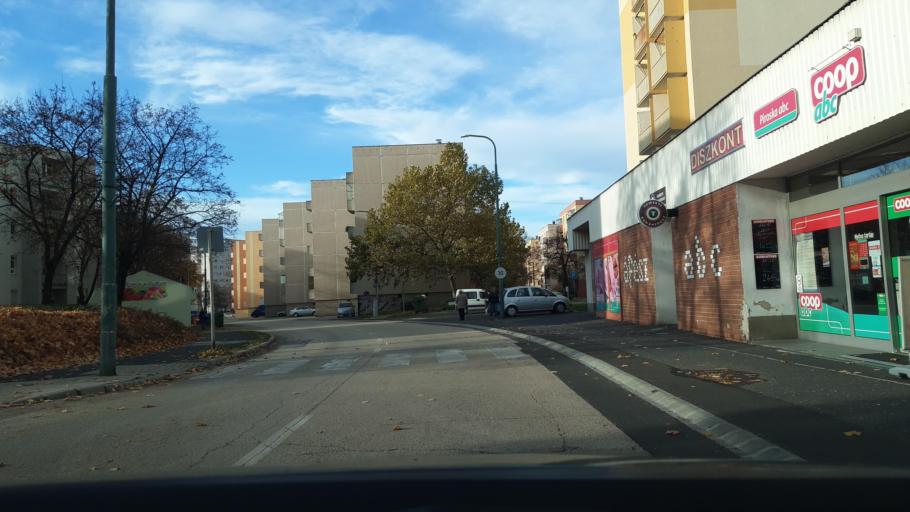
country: HU
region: Veszprem
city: Ajka
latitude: 47.1075
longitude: 17.5608
